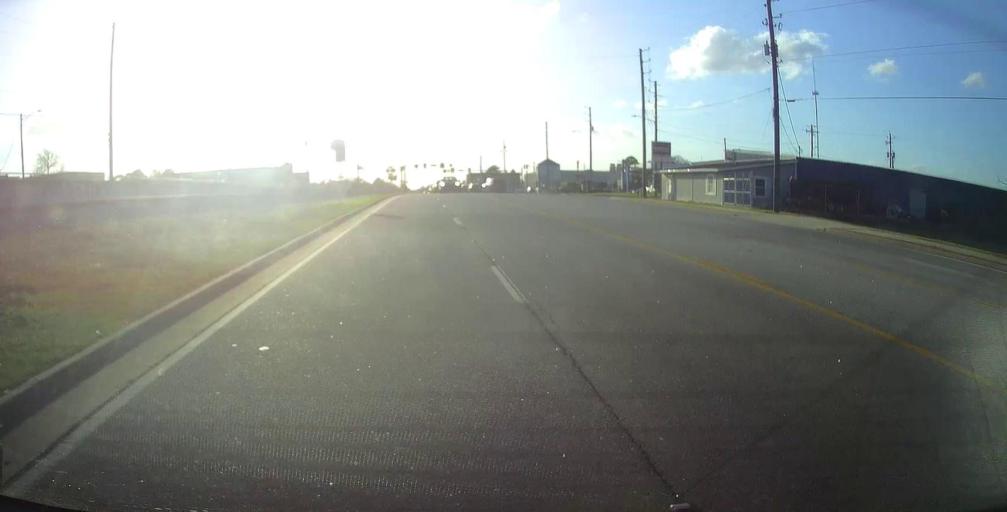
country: US
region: Georgia
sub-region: Evans County
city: Claxton
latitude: 32.1612
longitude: -81.9021
